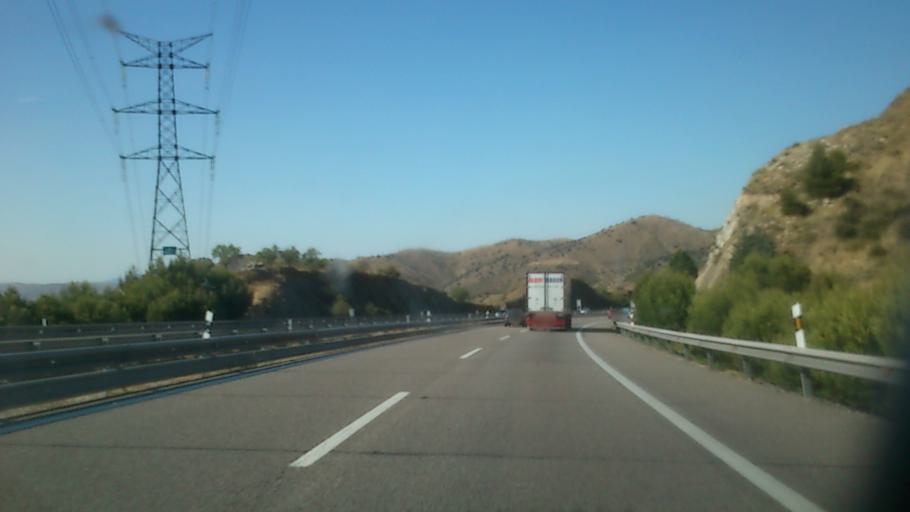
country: ES
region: Aragon
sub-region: Provincia de Zaragoza
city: Paracuellos de la Ribera
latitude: 41.3980
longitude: -1.5456
